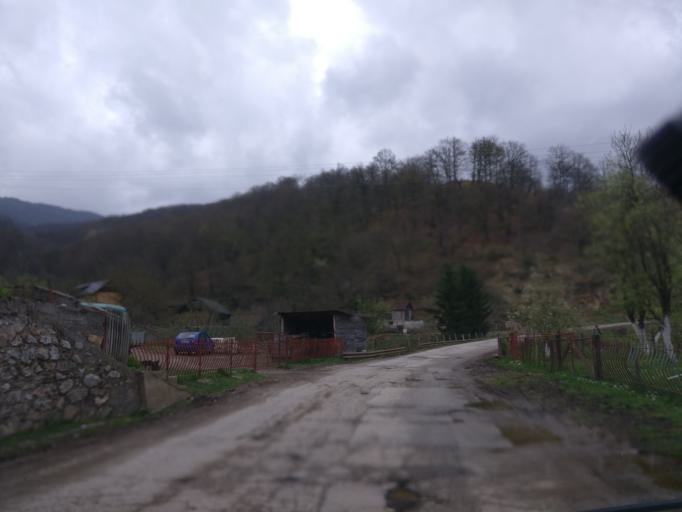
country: BA
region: Republika Srpska
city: Foca
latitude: 43.4402
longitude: 18.7620
